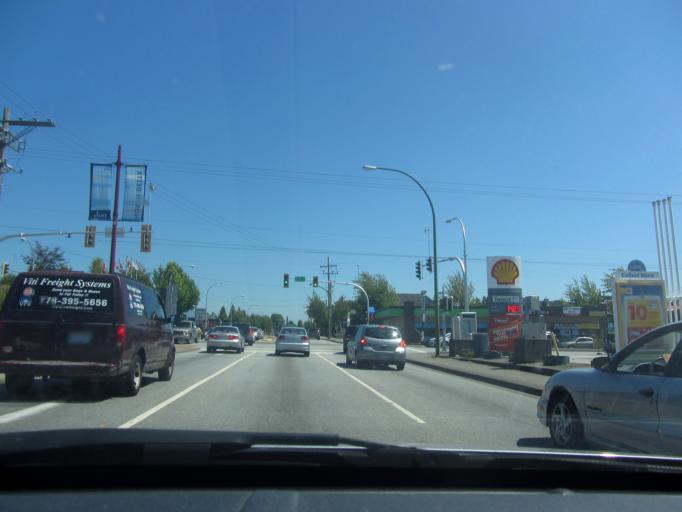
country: CA
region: British Columbia
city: Delta
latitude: 49.1340
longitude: -122.8911
